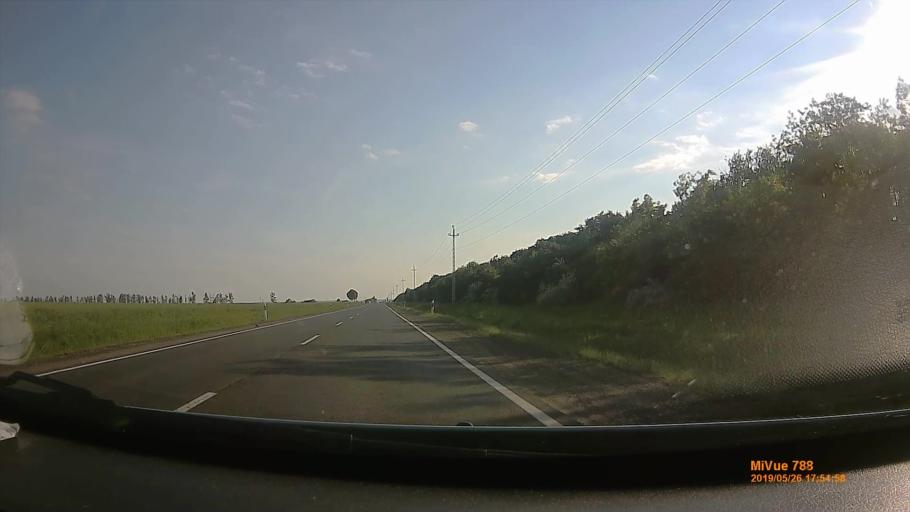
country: HU
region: Borsod-Abauj-Zemplen
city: Arnot
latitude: 48.1345
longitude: 20.8797
